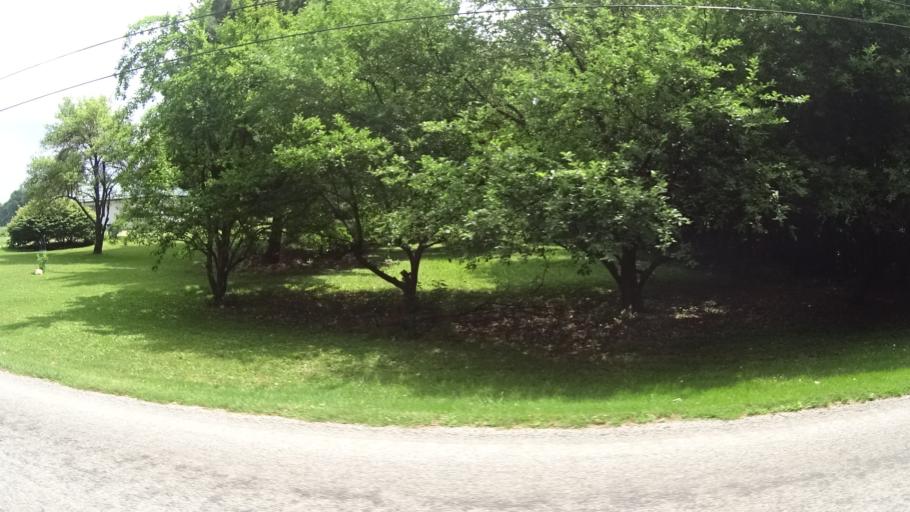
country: US
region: Ohio
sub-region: Lorain County
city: Vermilion
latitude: 41.3779
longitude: -82.3811
